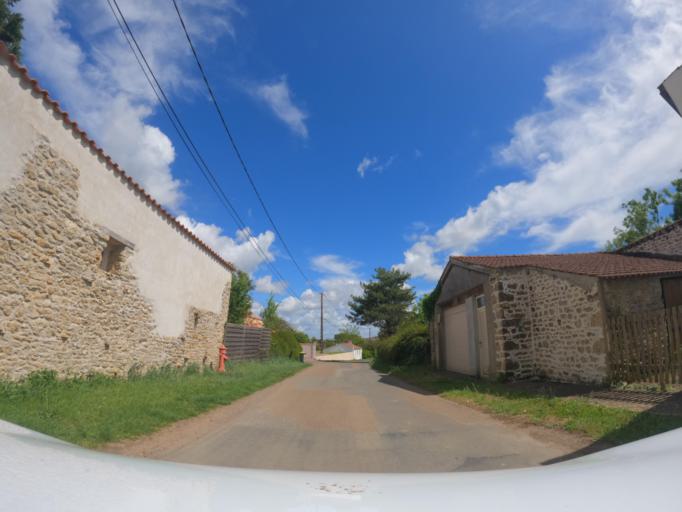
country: FR
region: Pays de la Loire
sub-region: Departement de la Vendee
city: Le Champ-Saint-Pere
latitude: 46.4904
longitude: -1.3259
